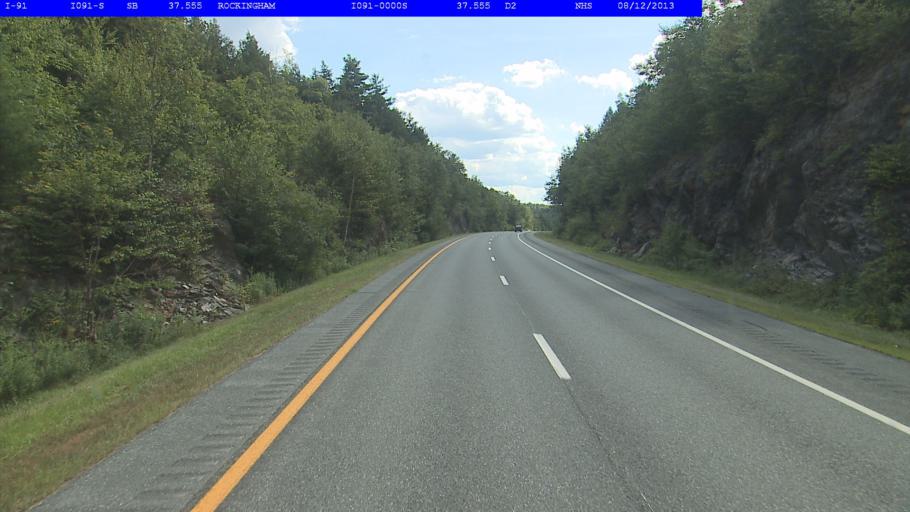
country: US
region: New Hampshire
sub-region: Sullivan County
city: Charlestown
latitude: 43.2116
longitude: -72.4539
